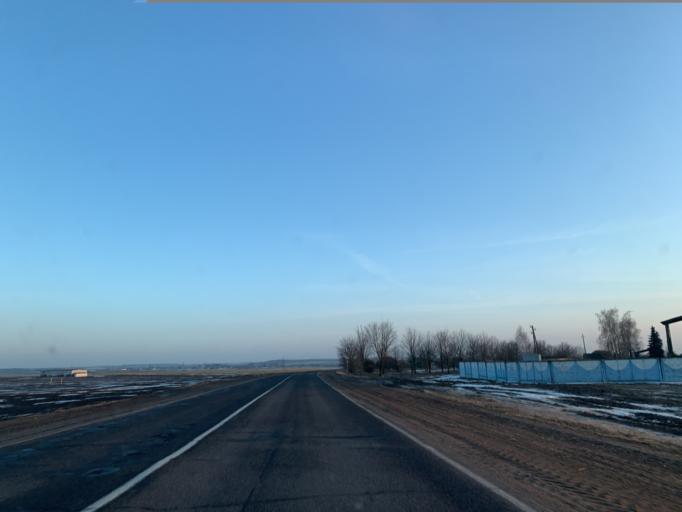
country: BY
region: Minsk
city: Haradzyeya
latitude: 53.3197
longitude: 26.5584
